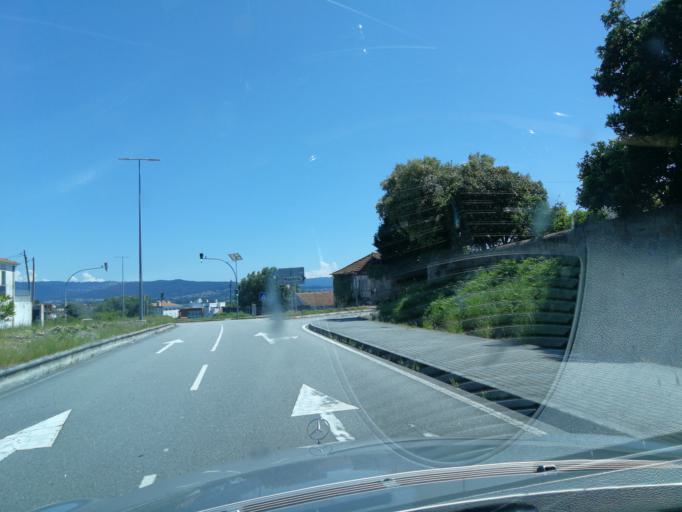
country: PT
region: Viana do Castelo
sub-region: Viana do Castelo
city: Meadela
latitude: 41.7099
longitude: -8.8076
